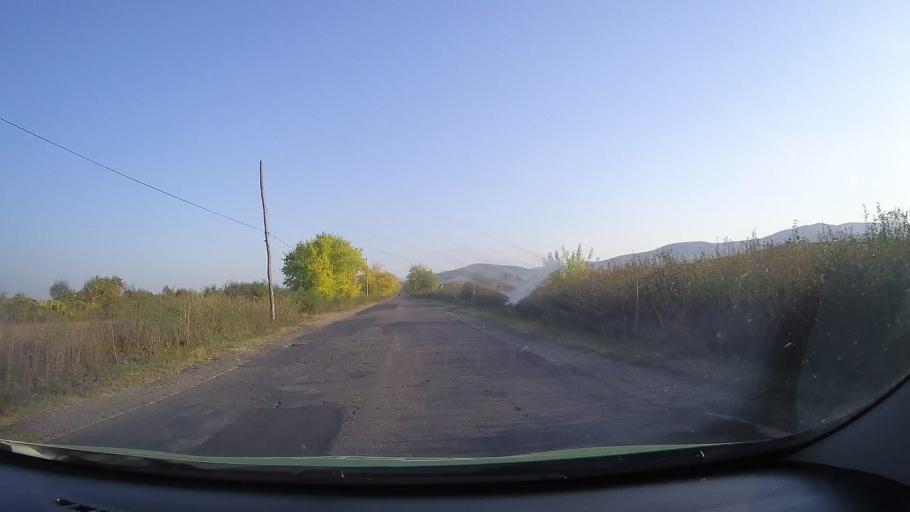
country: RO
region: Arad
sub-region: Comuna Pancota
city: Maderat
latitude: 46.3124
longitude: 21.7031
